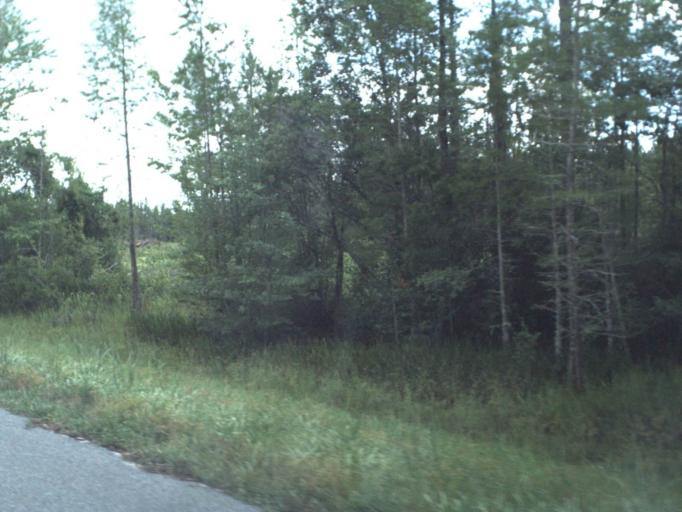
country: US
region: Florida
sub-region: Columbia County
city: Five Points
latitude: 30.3858
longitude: -82.6269
